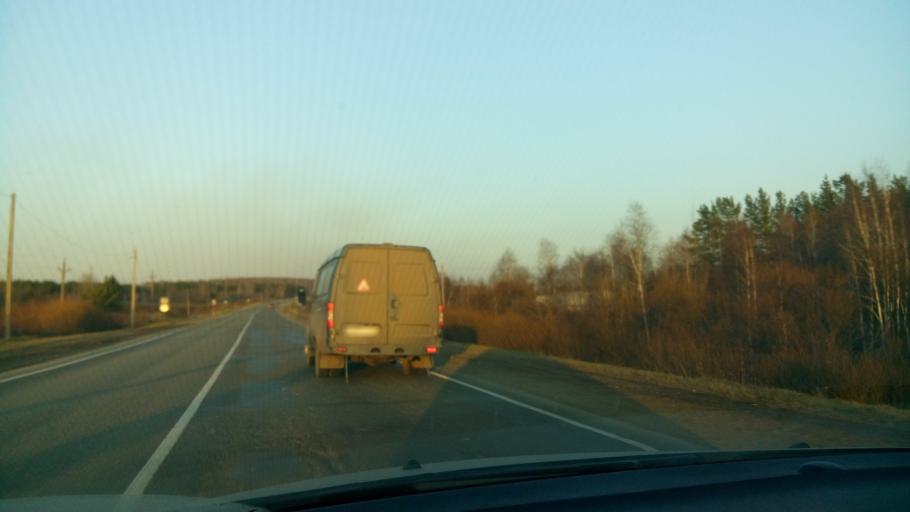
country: RU
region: Sverdlovsk
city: Obukhovskoye
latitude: 56.8515
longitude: 62.6038
